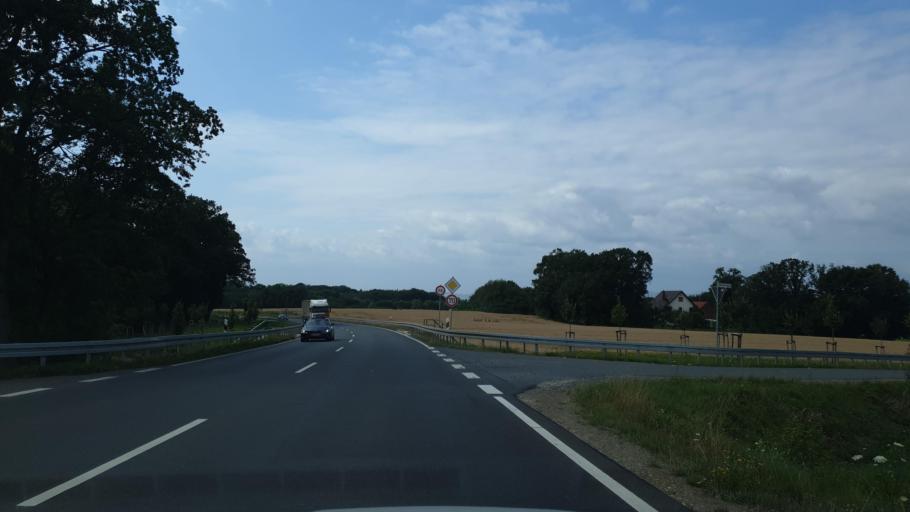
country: DE
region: North Rhine-Westphalia
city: Bad Oeynhausen
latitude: 52.1604
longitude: 8.7644
